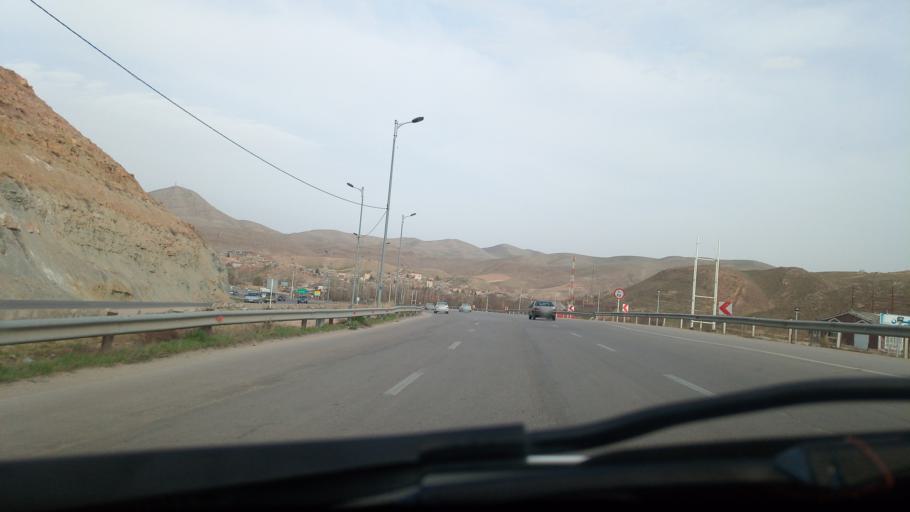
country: IR
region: Khorasan-e Shomali
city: Bojnurd
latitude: 37.4769
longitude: 57.4244
